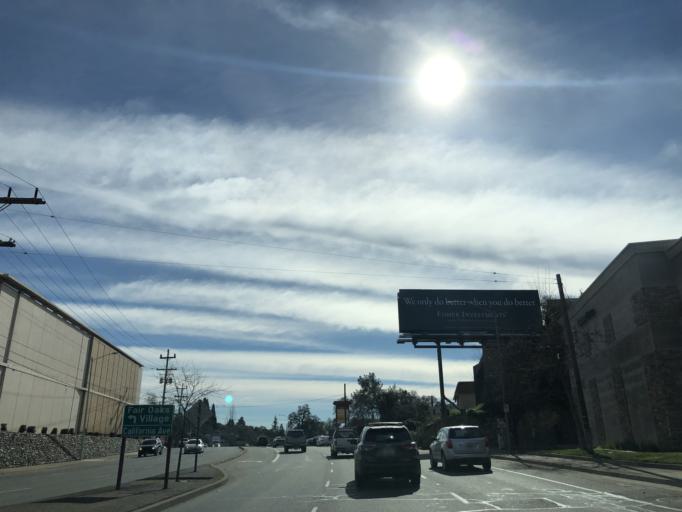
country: US
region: California
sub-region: Sacramento County
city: Fair Oaks
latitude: 38.6428
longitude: -121.2728
